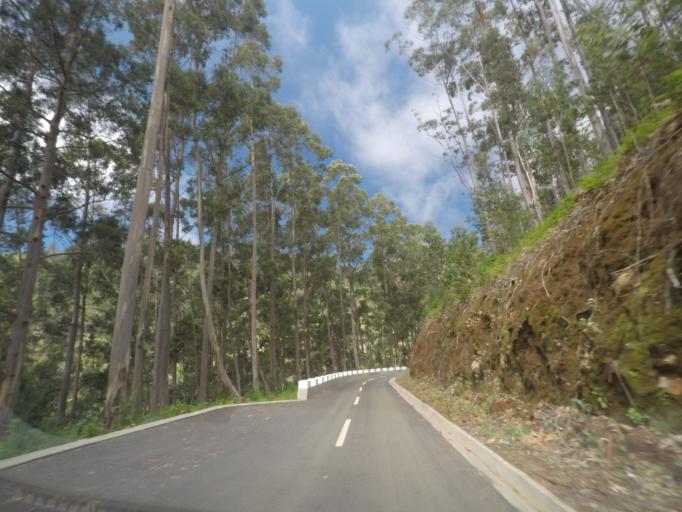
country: PT
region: Madeira
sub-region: Calheta
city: Arco da Calheta
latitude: 32.7258
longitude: -17.1234
